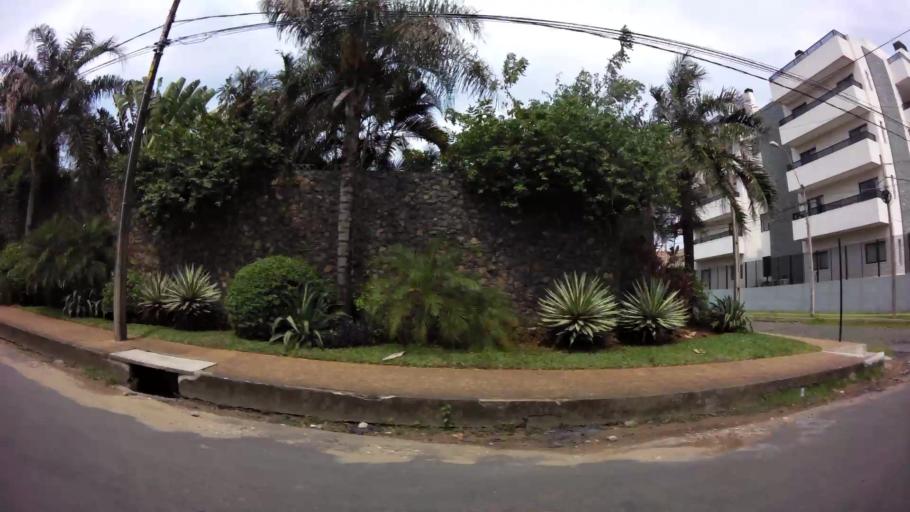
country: PY
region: Asuncion
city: Asuncion
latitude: -25.2808
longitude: -57.5795
